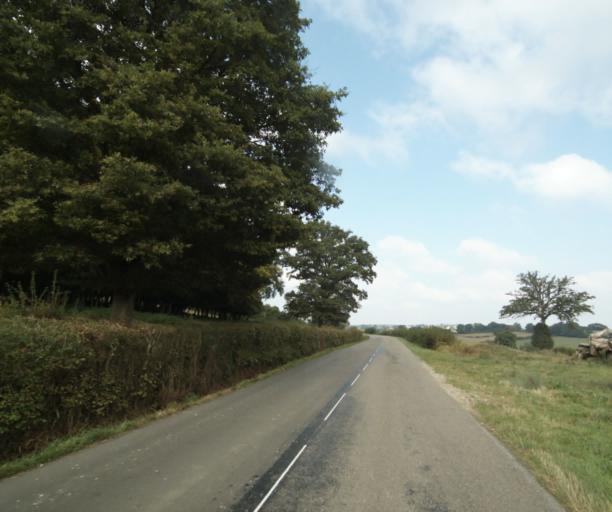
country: FR
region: Bourgogne
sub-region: Departement de Saone-et-Loire
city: Charolles
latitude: 46.4270
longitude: 4.3056
